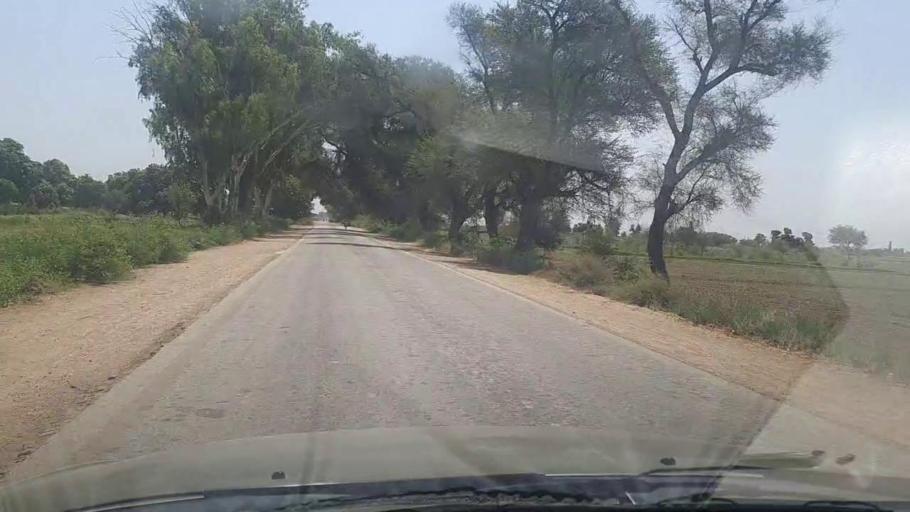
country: PK
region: Sindh
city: Hyderabad
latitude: 25.3764
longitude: 68.4608
